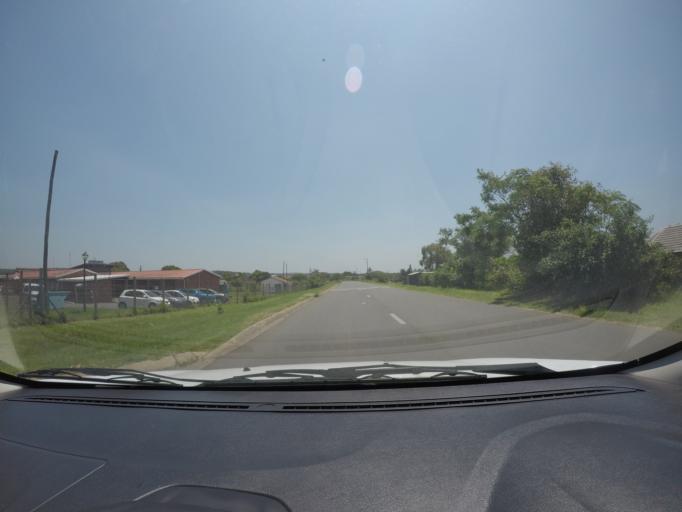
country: ZA
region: KwaZulu-Natal
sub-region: uThungulu District Municipality
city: eSikhawini
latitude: -28.8688
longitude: 31.9102
